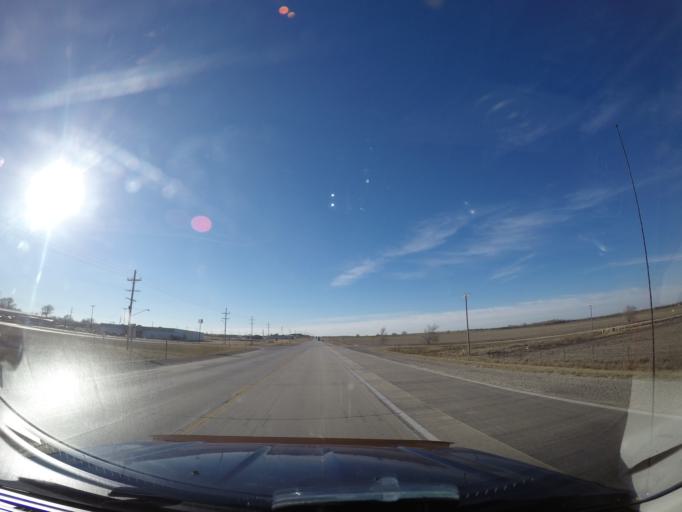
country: US
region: Kansas
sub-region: Marion County
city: Hillsboro
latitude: 38.3627
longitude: -97.2051
